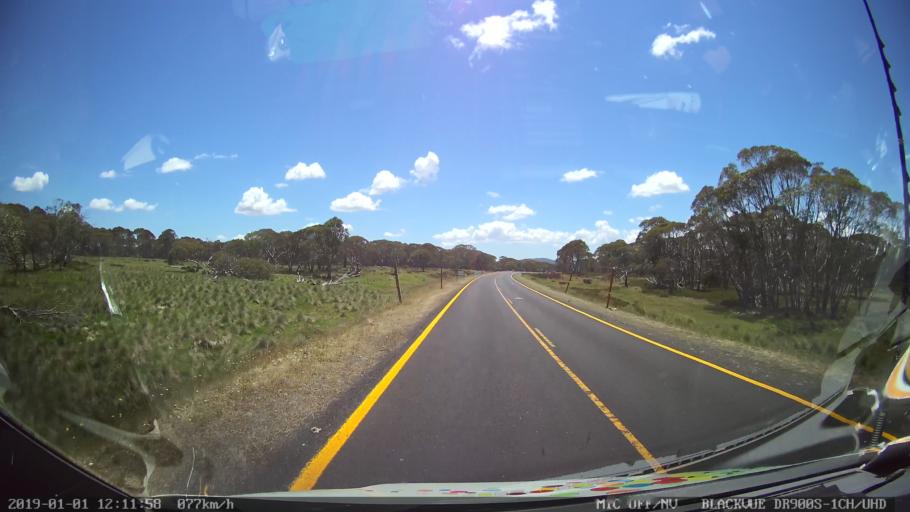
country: AU
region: New South Wales
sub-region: Tumut Shire
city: Tumut
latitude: -35.7780
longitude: 148.5106
